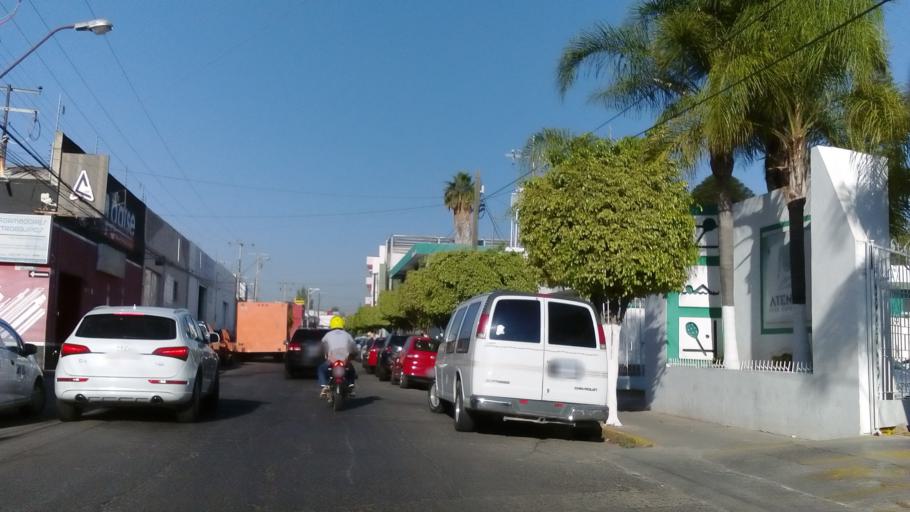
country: MX
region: Guanajuato
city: Leon
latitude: 21.1357
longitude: -101.6881
